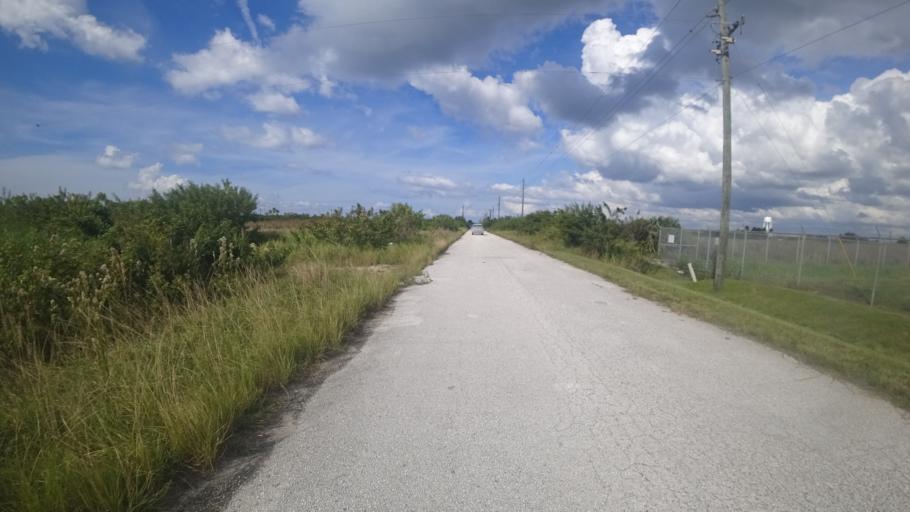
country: US
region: Florida
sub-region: Manatee County
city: Memphis
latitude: 27.6288
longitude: -82.5482
